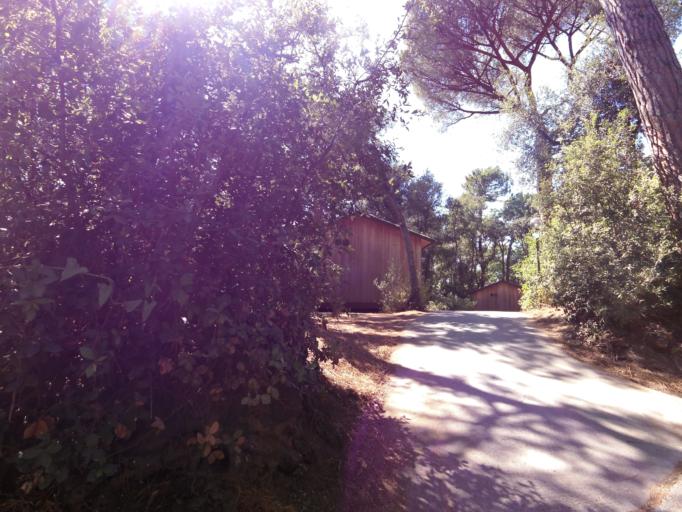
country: IT
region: Tuscany
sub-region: Provincia di Livorno
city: Donoratico
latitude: 43.1551
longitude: 10.5435
